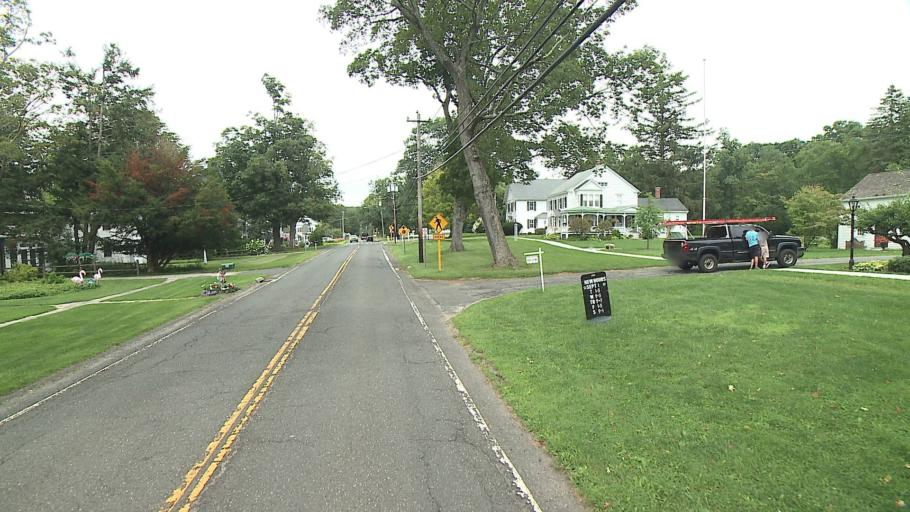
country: US
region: Connecticut
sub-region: Litchfield County
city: New Milford
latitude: 41.5333
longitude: -73.3657
